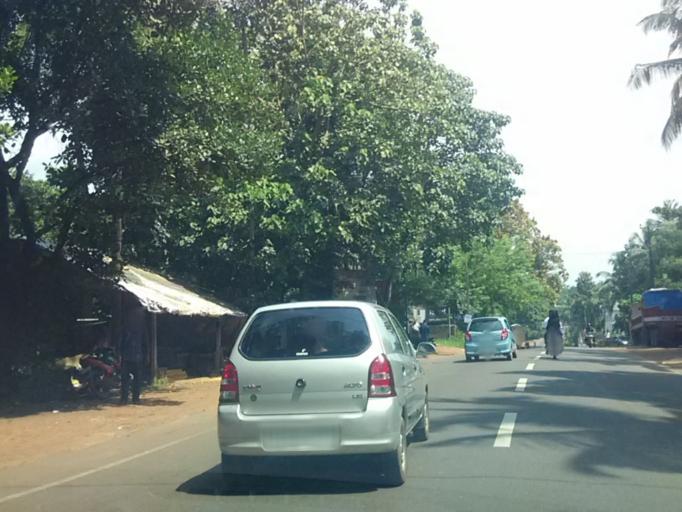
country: IN
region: Kerala
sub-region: Kozhikode
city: Kunnamangalam
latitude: 11.3185
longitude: 75.8844
